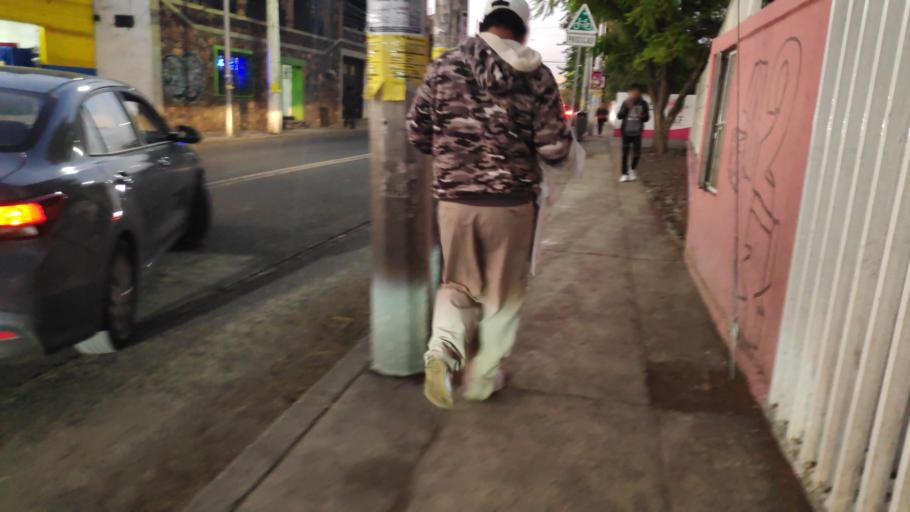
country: MX
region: Queretaro
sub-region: Queretaro
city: Santiago de Queretaro
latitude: 20.5884
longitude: -100.3765
